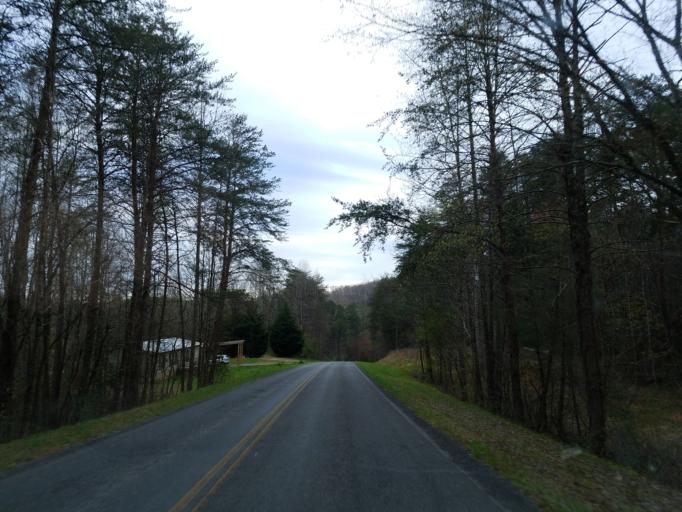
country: US
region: Georgia
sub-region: Fannin County
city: Blue Ridge
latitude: 34.6915
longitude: -84.2999
